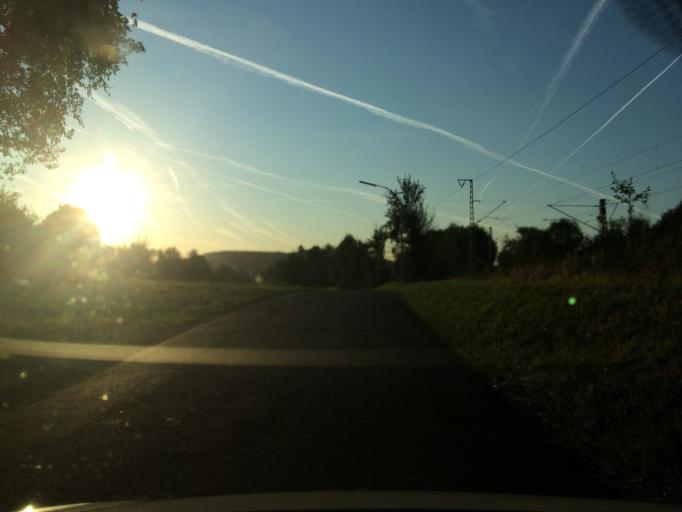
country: DE
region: Bavaria
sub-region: Regierungsbezirk Unterfranken
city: Hosbach
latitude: 50.0013
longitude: 9.2197
